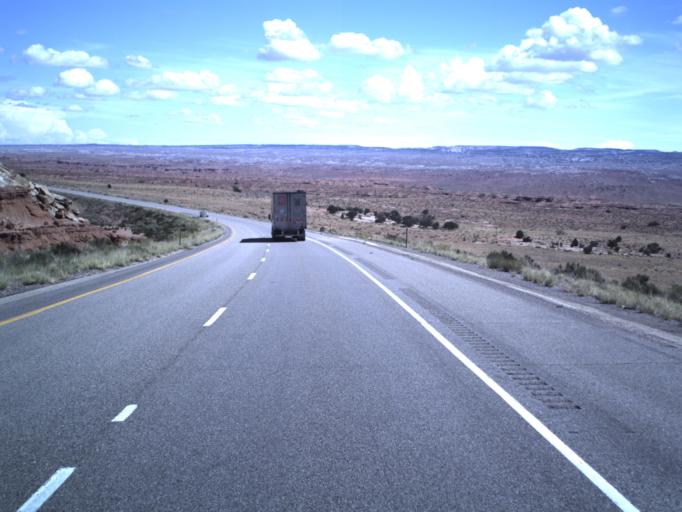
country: US
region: Utah
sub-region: Emery County
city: Ferron
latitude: 38.8302
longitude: -111.1126
